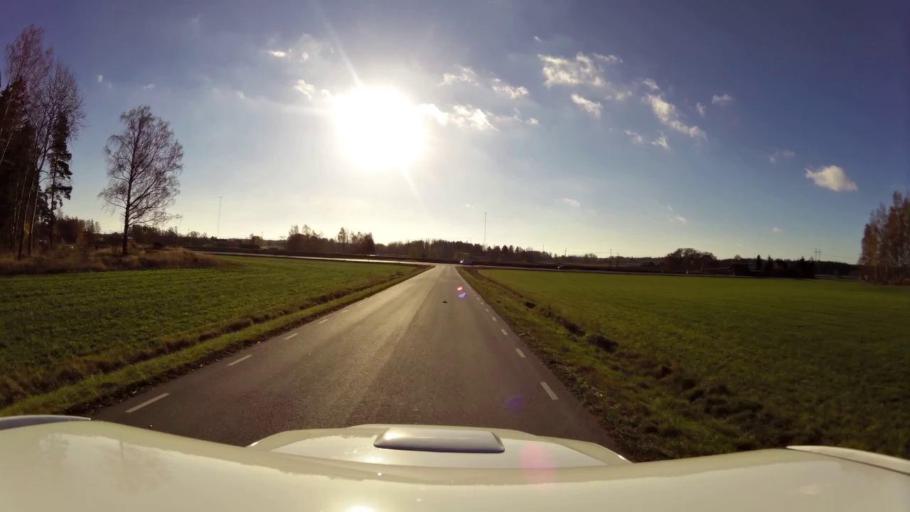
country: SE
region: OEstergoetland
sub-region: Linkopings Kommun
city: Linghem
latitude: 58.4378
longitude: 15.7769
